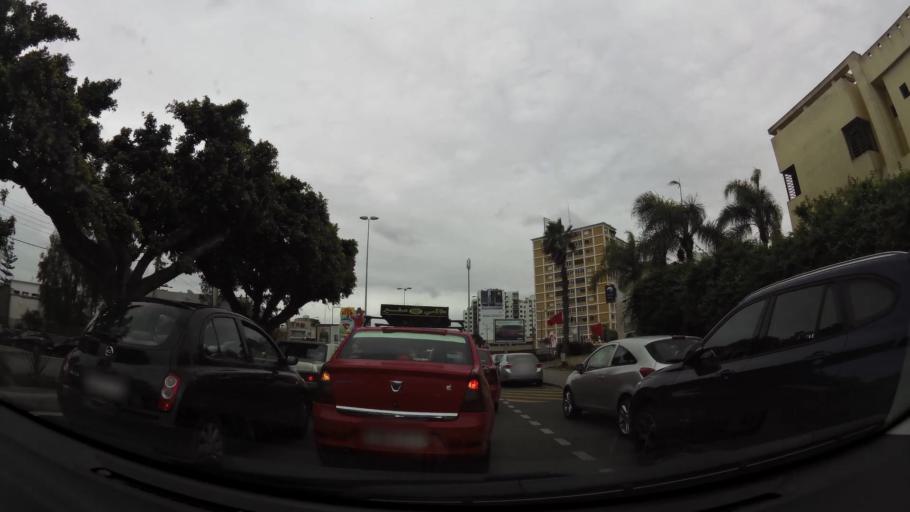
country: MA
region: Grand Casablanca
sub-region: Casablanca
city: Casablanca
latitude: 33.5875
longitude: -7.6496
